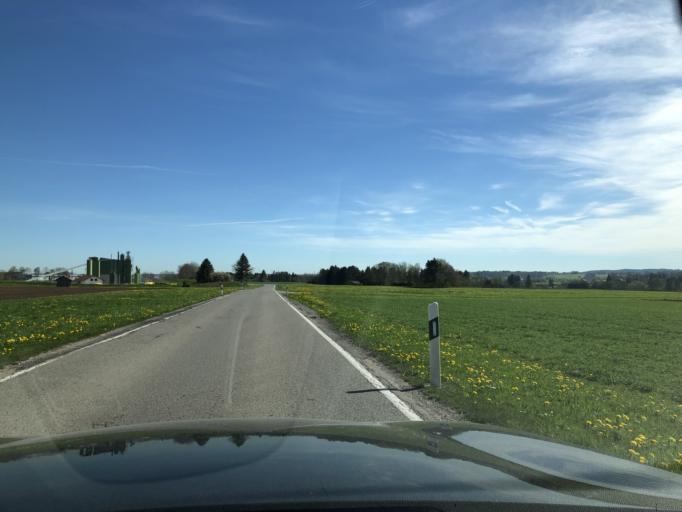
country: DE
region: Bavaria
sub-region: Swabia
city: Marktoberdorf
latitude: 47.7629
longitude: 10.5758
